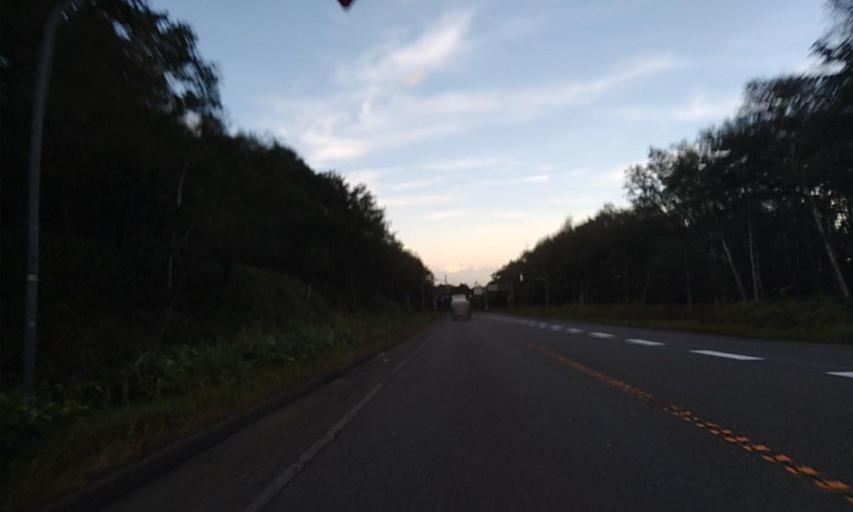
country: JP
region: Hokkaido
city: Otofuke
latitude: 42.9629
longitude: 142.7976
